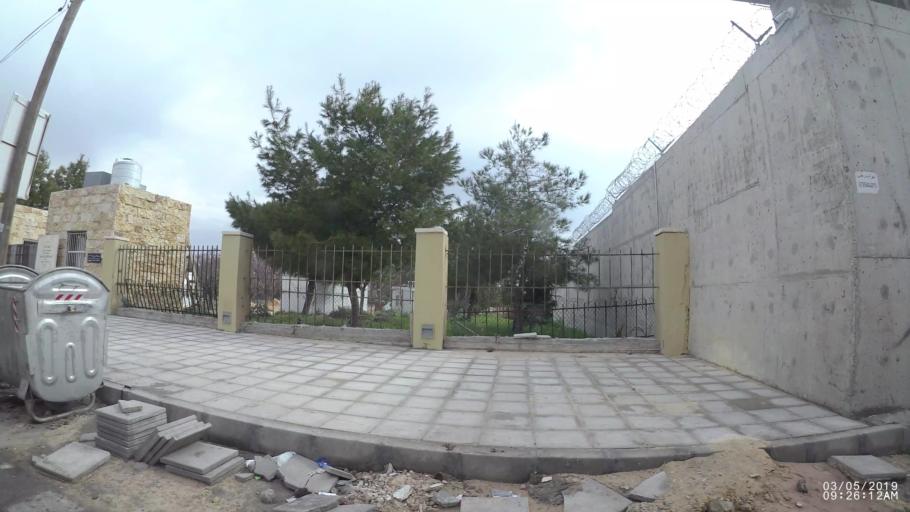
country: JO
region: Amman
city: Amman
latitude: 31.9697
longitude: 35.9348
